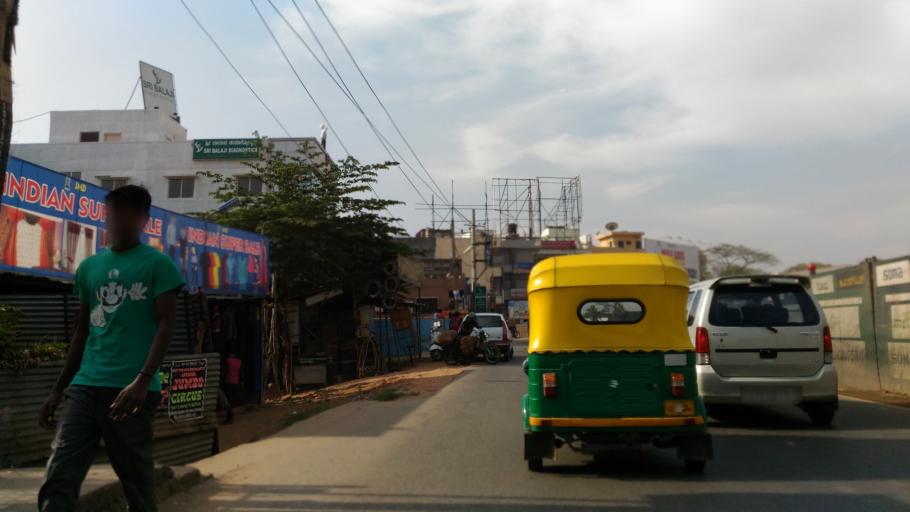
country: IN
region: Karnataka
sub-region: Bangalore Urban
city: Bangalore
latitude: 12.9113
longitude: 77.4848
